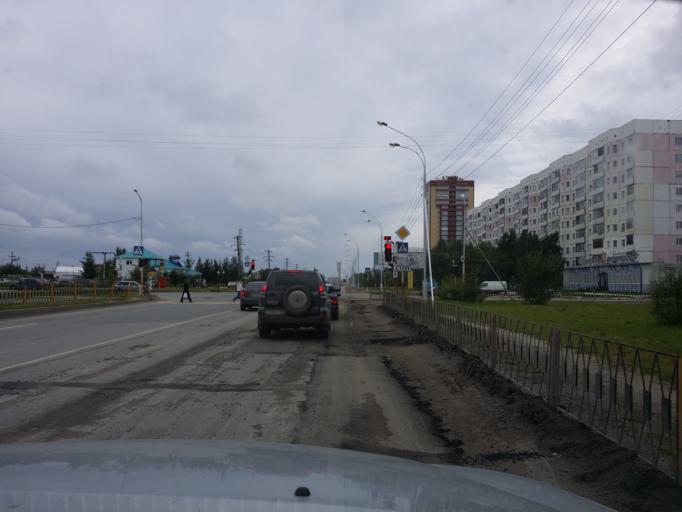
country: RU
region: Khanty-Mansiyskiy Avtonomnyy Okrug
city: Nizhnevartovsk
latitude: 60.9292
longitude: 76.6069
